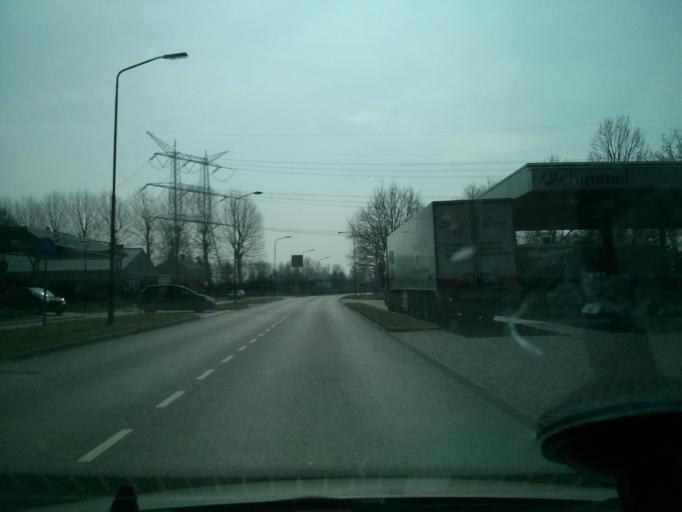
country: NL
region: North Brabant
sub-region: Gemeente Son en Breugel
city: Son
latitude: 51.5015
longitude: 5.4942
